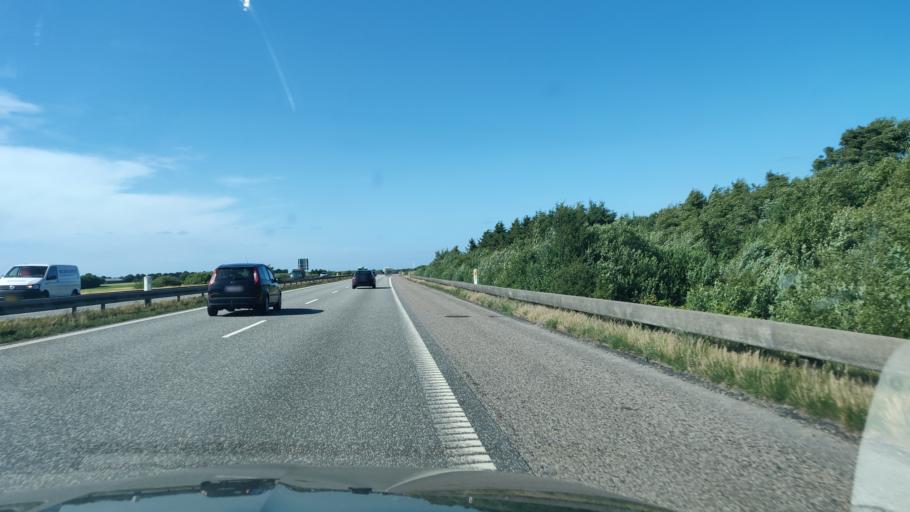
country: DK
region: North Denmark
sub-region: Mariagerfjord Kommune
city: Hobro
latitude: 56.7496
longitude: 9.6963
